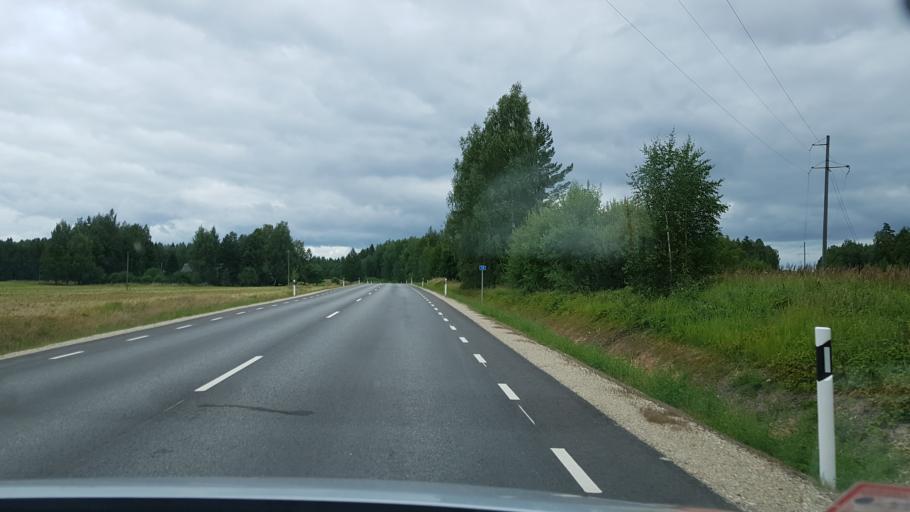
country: EE
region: Polvamaa
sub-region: Raepina vald
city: Rapina
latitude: 58.0739
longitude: 27.2905
